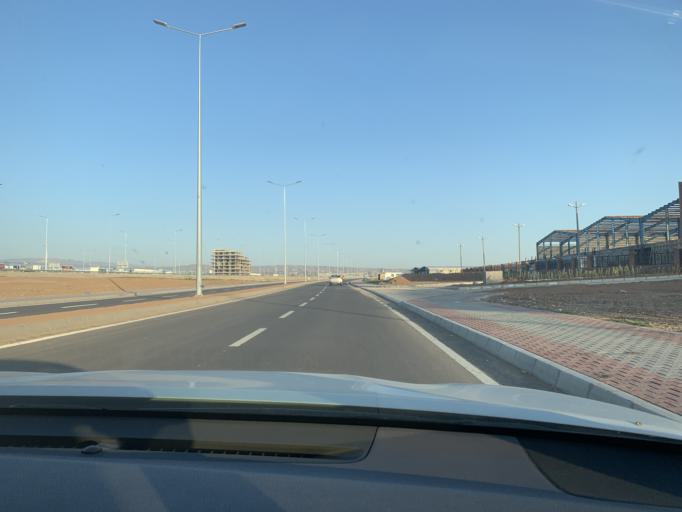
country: IQ
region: Arbil
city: Erbil
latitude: 36.2853
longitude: 44.0466
